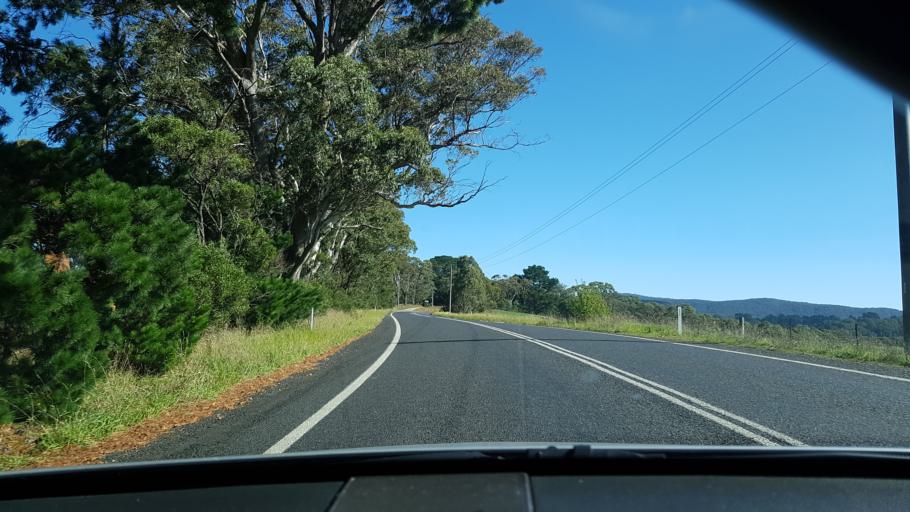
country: AU
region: New South Wales
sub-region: Lithgow
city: Bowenfels
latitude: -33.6372
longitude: 150.0653
